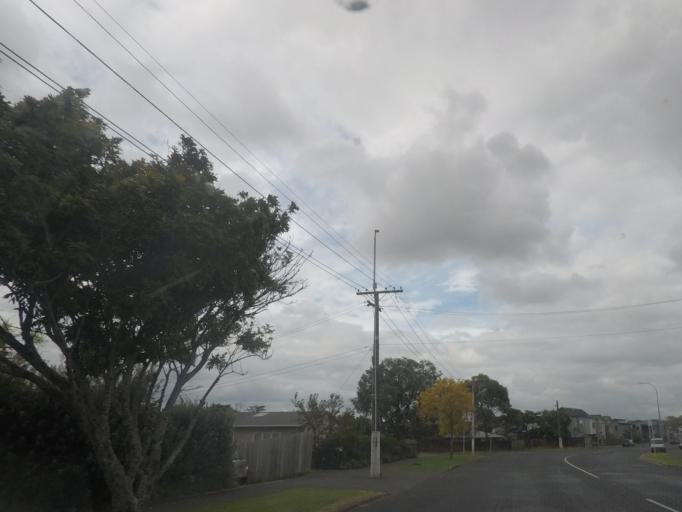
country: NZ
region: Auckland
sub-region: Auckland
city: Tamaki
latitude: -36.8753
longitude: 174.8733
